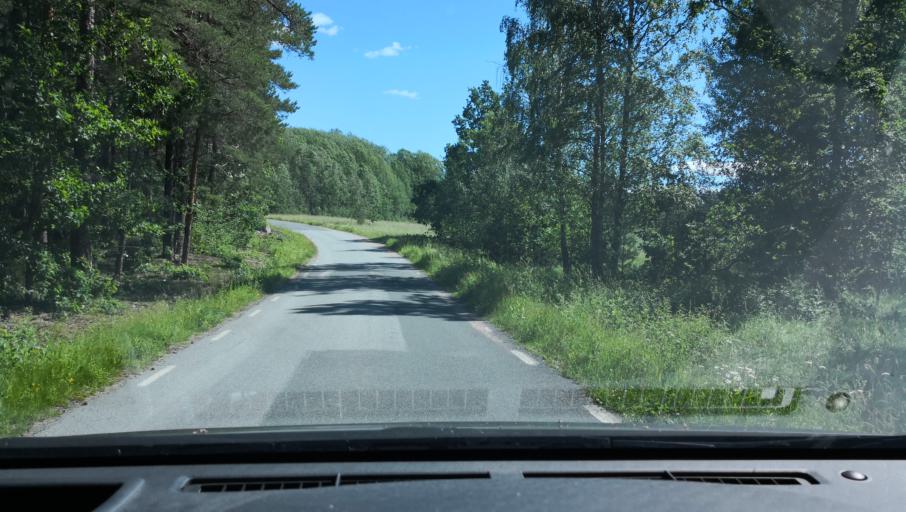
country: SE
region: Soedermanland
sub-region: Eskilstuna Kommun
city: Hallbybrunn
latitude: 59.3061
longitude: 16.3691
